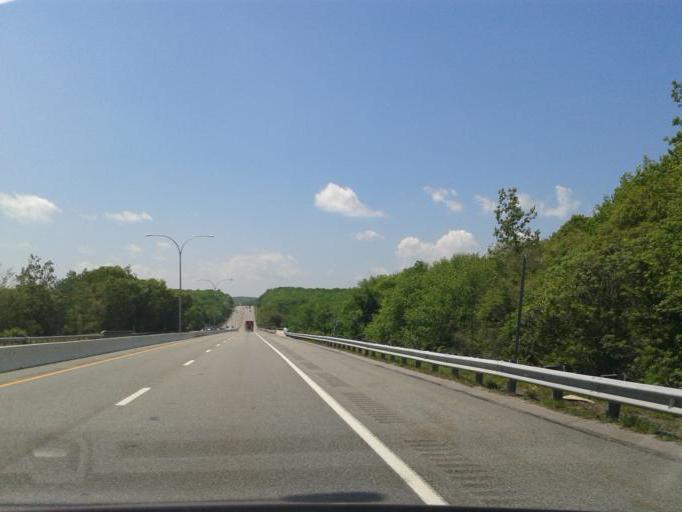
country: US
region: Rhode Island
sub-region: Washington County
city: North Kingstown
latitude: 41.5276
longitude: -71.4383
